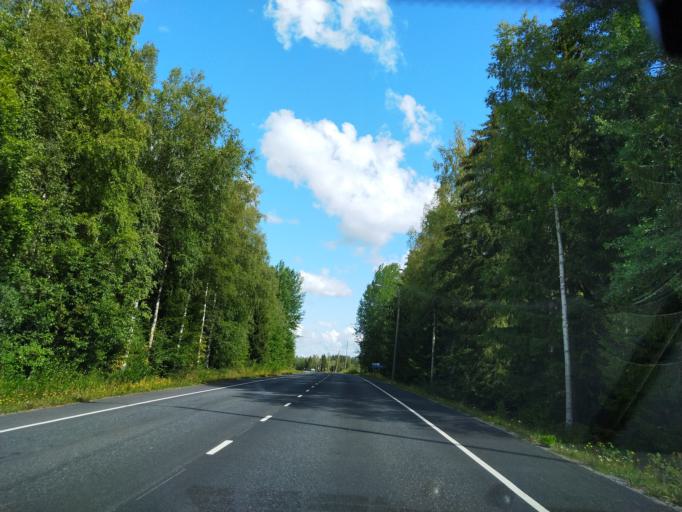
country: FI
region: Satakunta
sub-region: Pori
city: Huittinen
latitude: 61.1758
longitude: 22.7115
